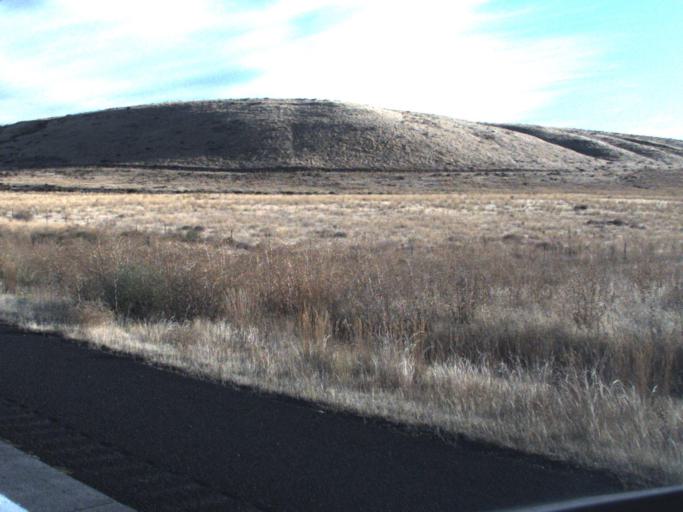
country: US
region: Washington
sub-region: Franklin County
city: Connell
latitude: 46.6806
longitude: -118.8424
